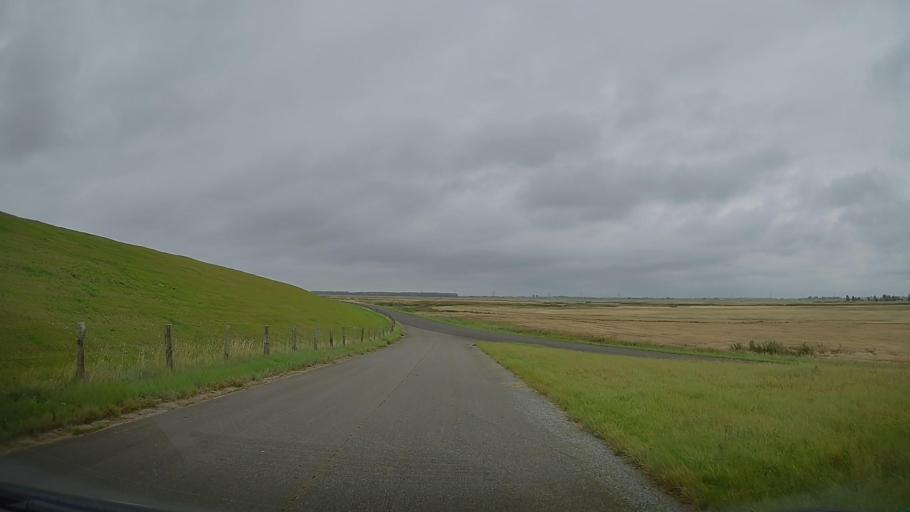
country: DE
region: Schleswig-Holstein
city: Busenwurth
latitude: 54.0394
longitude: 8.9766
